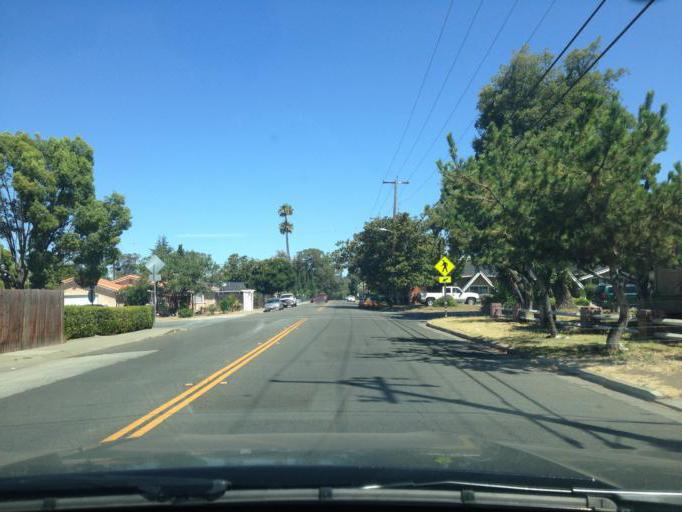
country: US
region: California
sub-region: Santa Clara County
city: East Foothills
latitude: 37.3896
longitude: -121.8321
